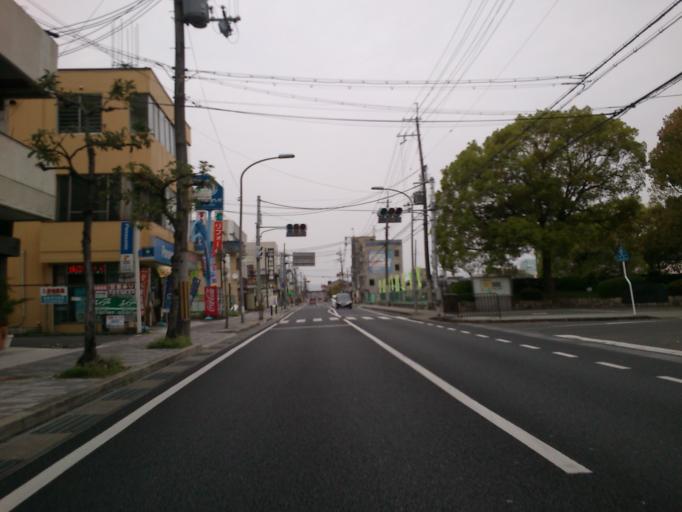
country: JP
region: Kyoto
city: Yawata
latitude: 34.8750
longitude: 135.7065
